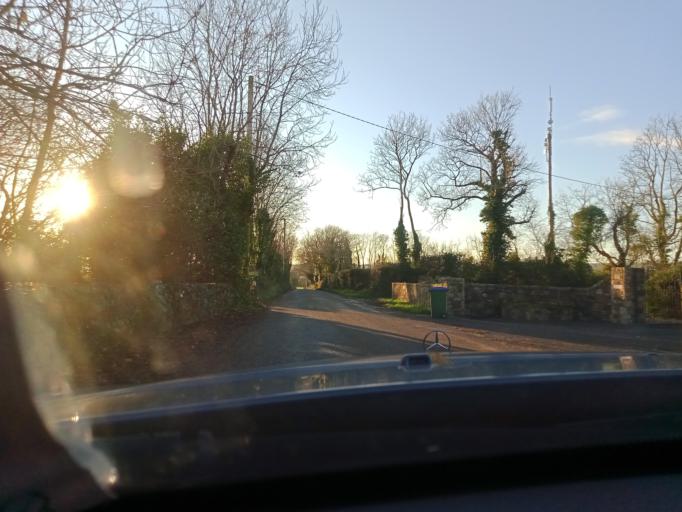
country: IE
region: Leinster
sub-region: Loch Garman
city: New Ross
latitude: 52.3939
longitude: -6.9658
